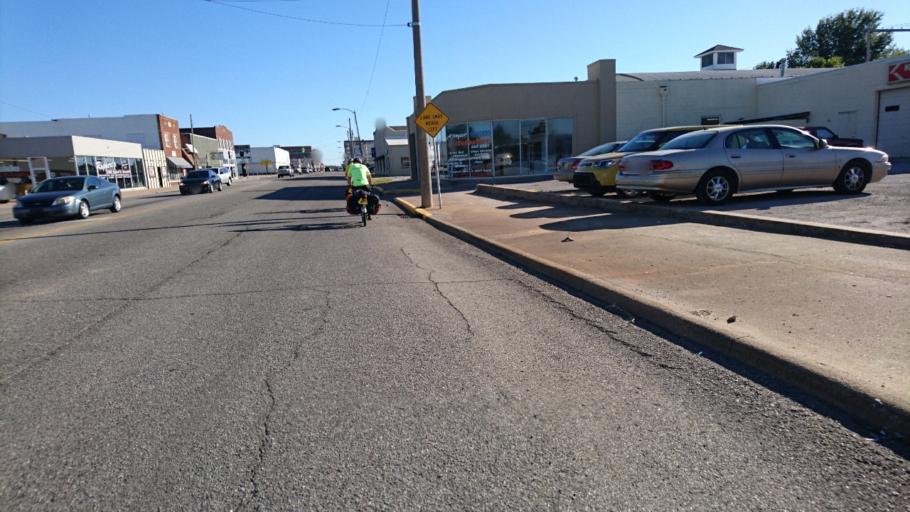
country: US
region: Oklahoma
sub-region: Ottawa County
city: Miami
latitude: 36.8802
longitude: -94.8776
